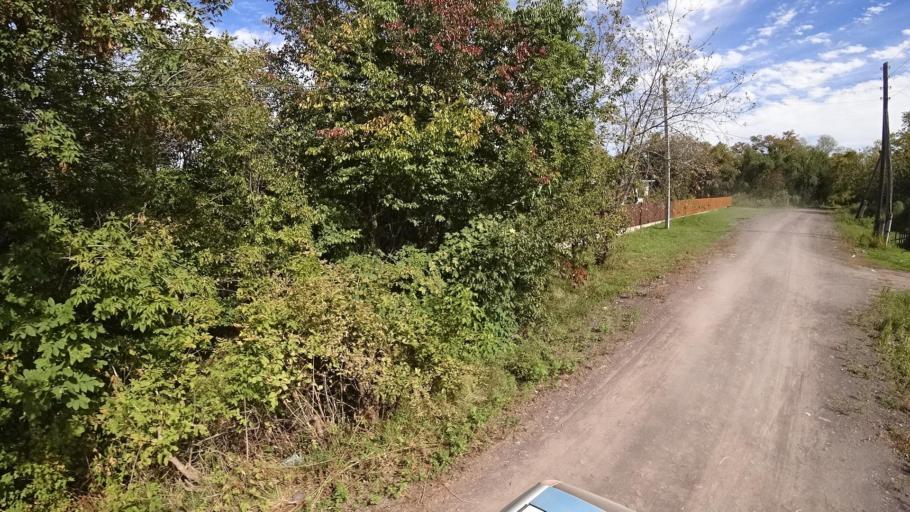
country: RU
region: Primorskiy
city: Yakovlevka
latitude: 44.4303
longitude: 133.5740
